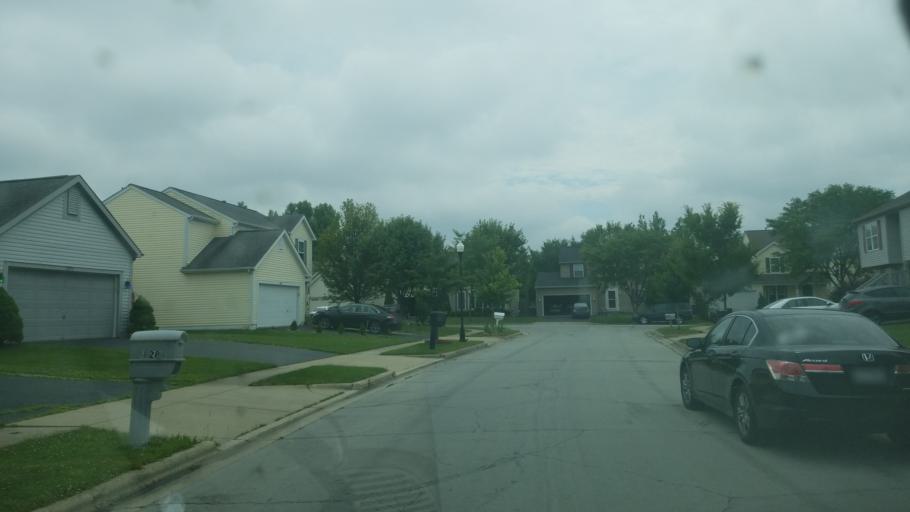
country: US
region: Ohio
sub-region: Franklin County
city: Reynoldsburg
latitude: 40.0009
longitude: -82.7848
